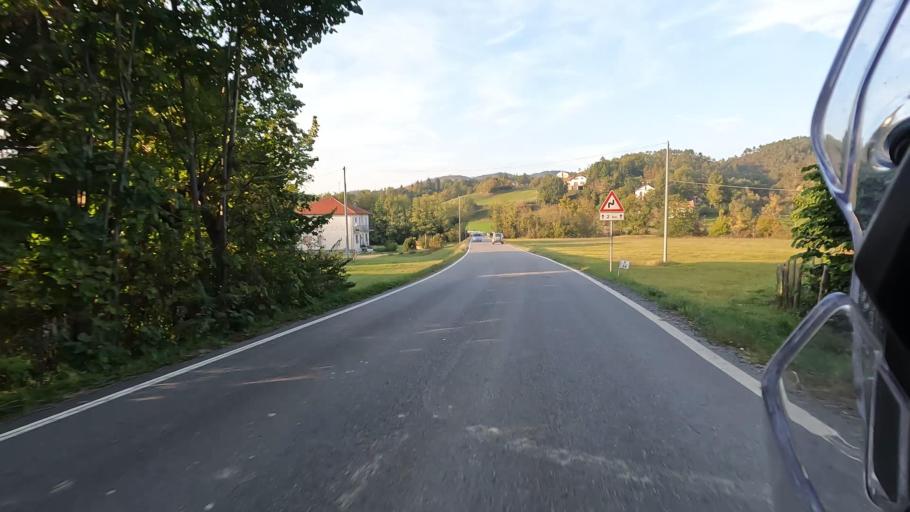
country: IT
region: Liguria
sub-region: Provincia di Savona
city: Sassello
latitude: 44.4958
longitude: 8.4963
